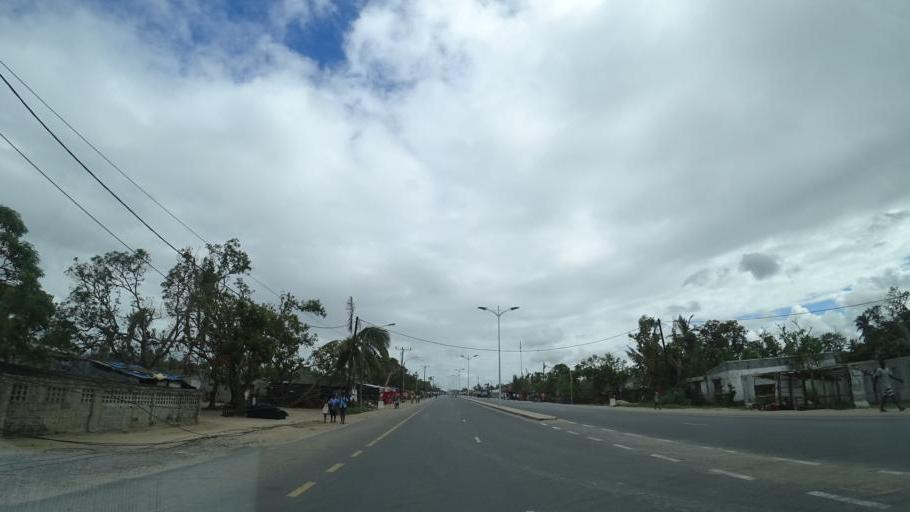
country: MZ
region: Sofala
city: Beira
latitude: -19.7262
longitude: 34.8154
